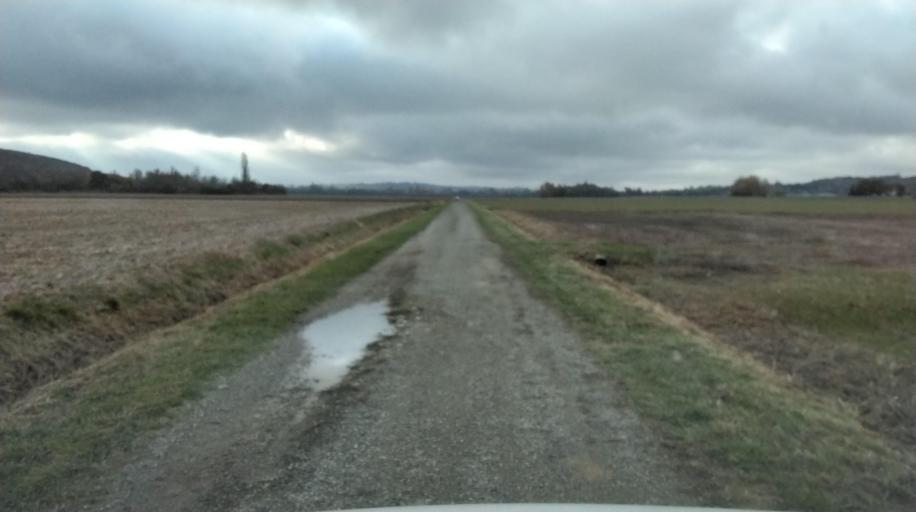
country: FR
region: Midi-Pyrenees
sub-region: Departement de la Haute-Garonne
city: Le Fousseret
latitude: 43.2688
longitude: 1.0481
